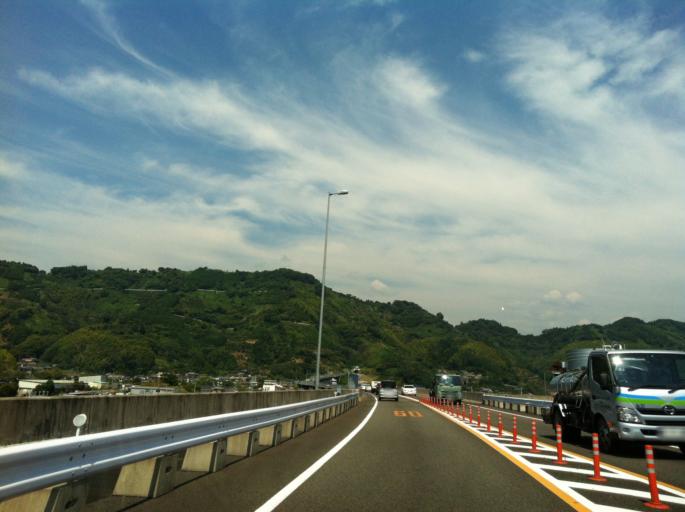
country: JP
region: Shizuoka
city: Shizuoka-shi
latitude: 35.0170
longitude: 138.3948
